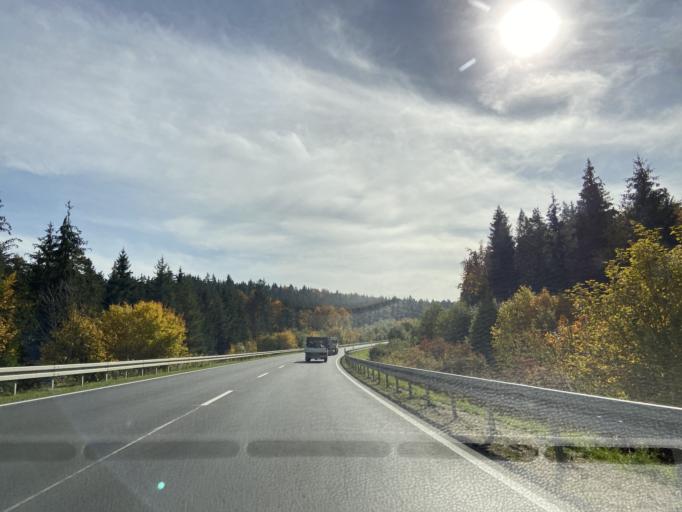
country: DE
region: Baden-Wuerttemberg
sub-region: Tuebingen Region
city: Inzigkofen
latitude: 48.1309
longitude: 9.1658
